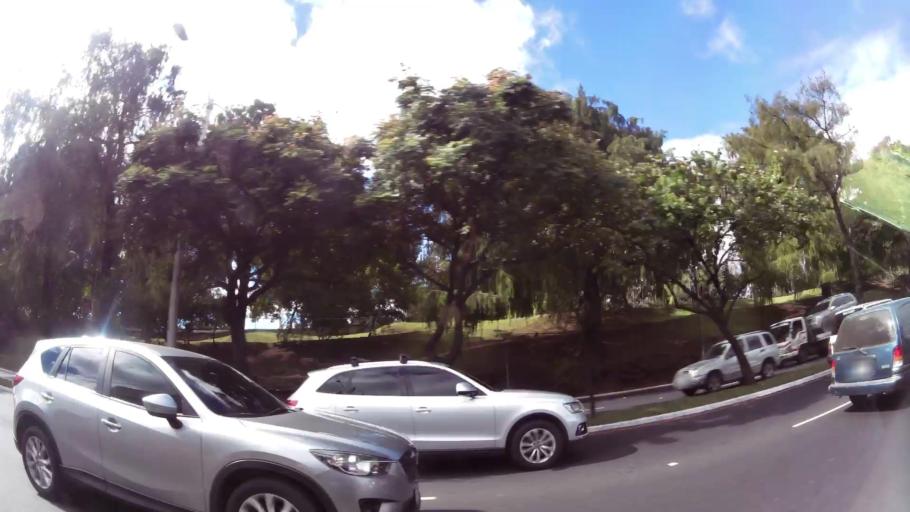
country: GT
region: Guatemala
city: Guatemala City
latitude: 14.6005
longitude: -90.5256
